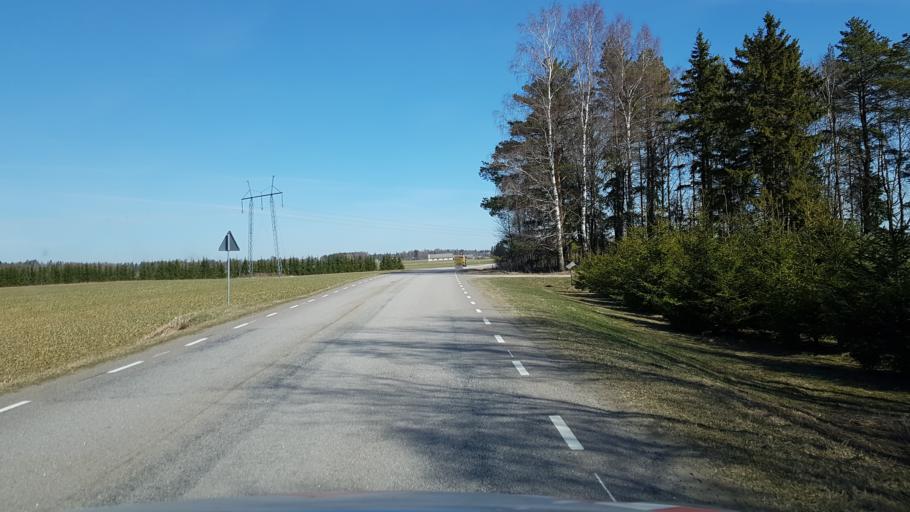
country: EE
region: Laeaene-Virumaa
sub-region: Vinni vald
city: Vinni
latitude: 59.2442
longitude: 26.3524
